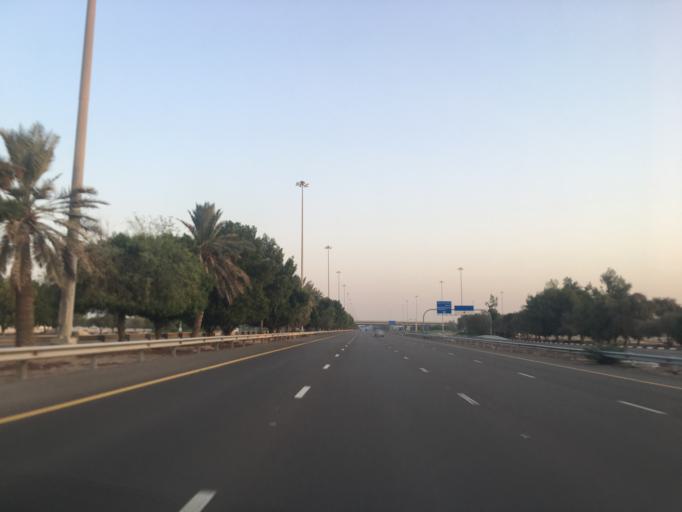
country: AE
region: Abu Dhabi
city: Abu Dhabi
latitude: 24.3712
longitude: 54.5560
